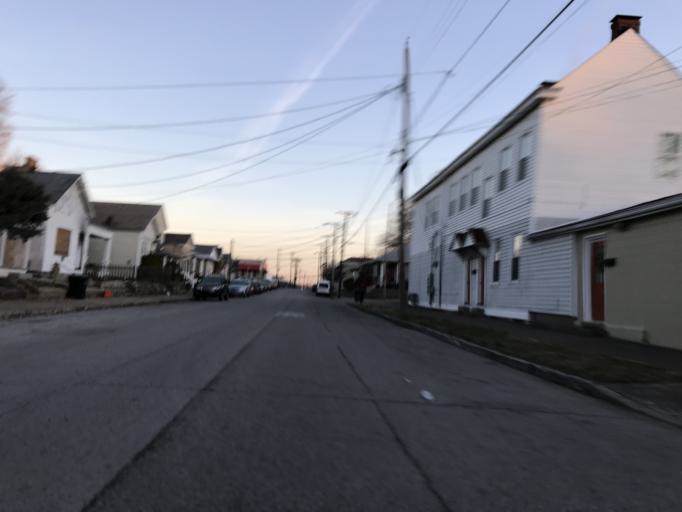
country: US
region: Kentucky
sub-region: Jefferson County
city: Louisville
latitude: 38.2379
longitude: -85.7368
